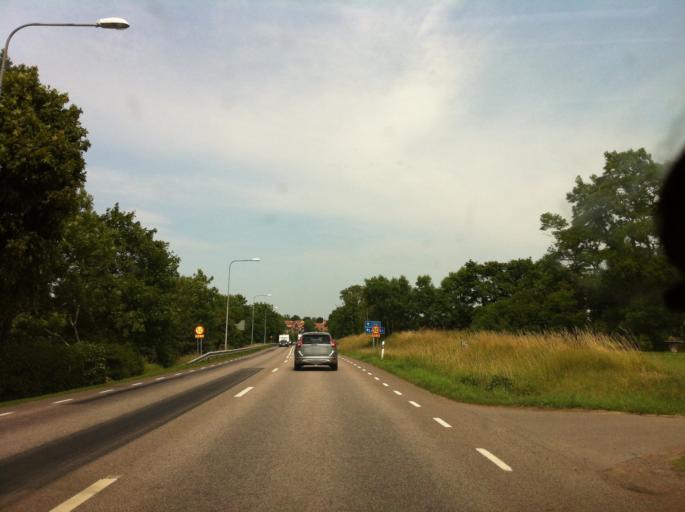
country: SE
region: Kalmar
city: Faerjestaden
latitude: 56.7144
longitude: 16.5330
